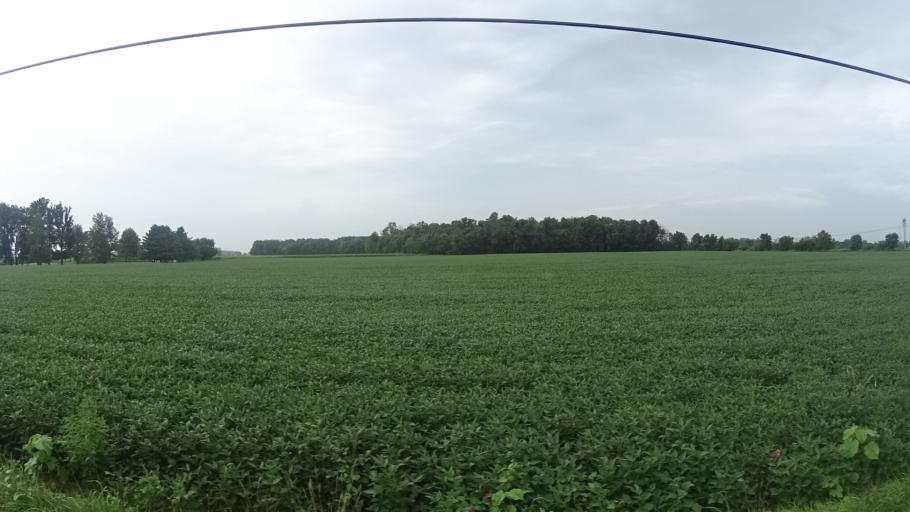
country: US
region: Indiana
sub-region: Madison County
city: Lapel
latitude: 40.0165
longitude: -85.8259
